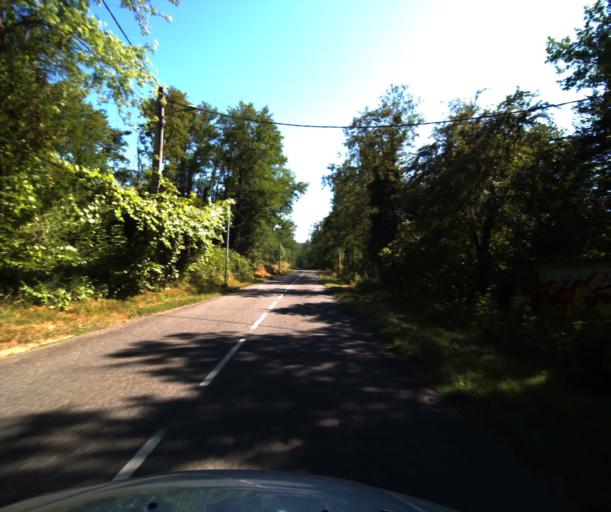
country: FR
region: Midi-Pyrenees
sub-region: Departement de la Haute-Garonne
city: Eaunes
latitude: 43.4376
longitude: 1.3269
